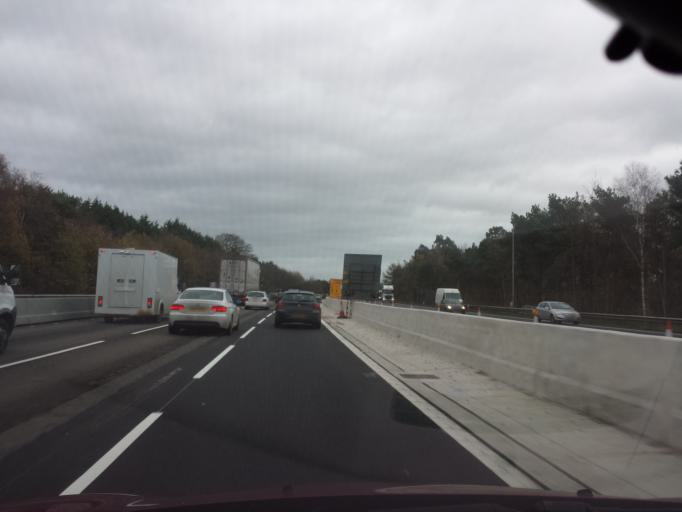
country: GB
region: England
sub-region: Surrey
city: Windlesham
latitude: 51.3658
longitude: -0.6374
